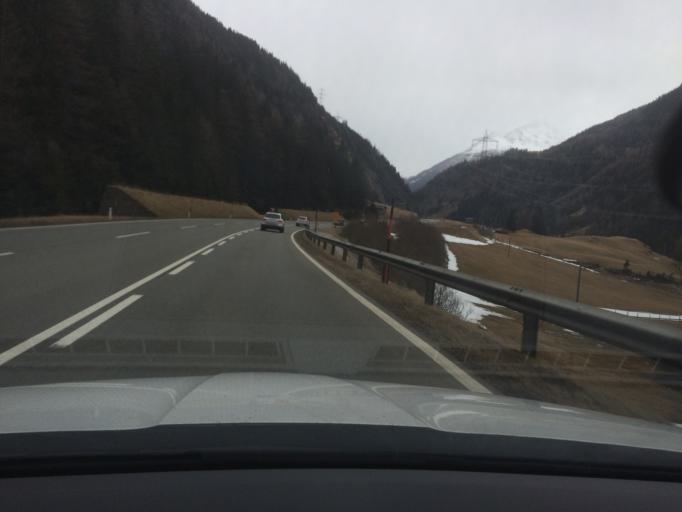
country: AT
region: Tyrol
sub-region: Politischer Bezirk Lienz
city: Matrei in Osttirol
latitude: 47.0414
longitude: 12.5166
